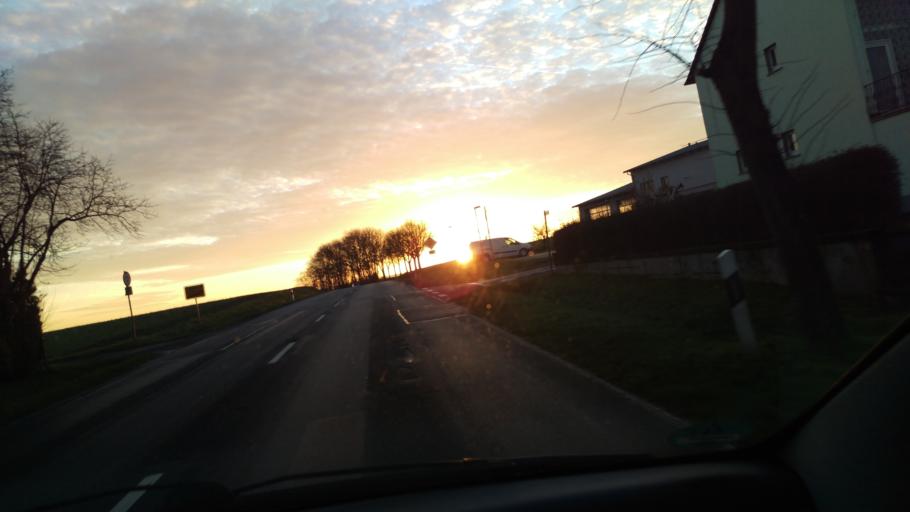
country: DE
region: Hesse
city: Romrod
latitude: 50.7615
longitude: 9.2119
